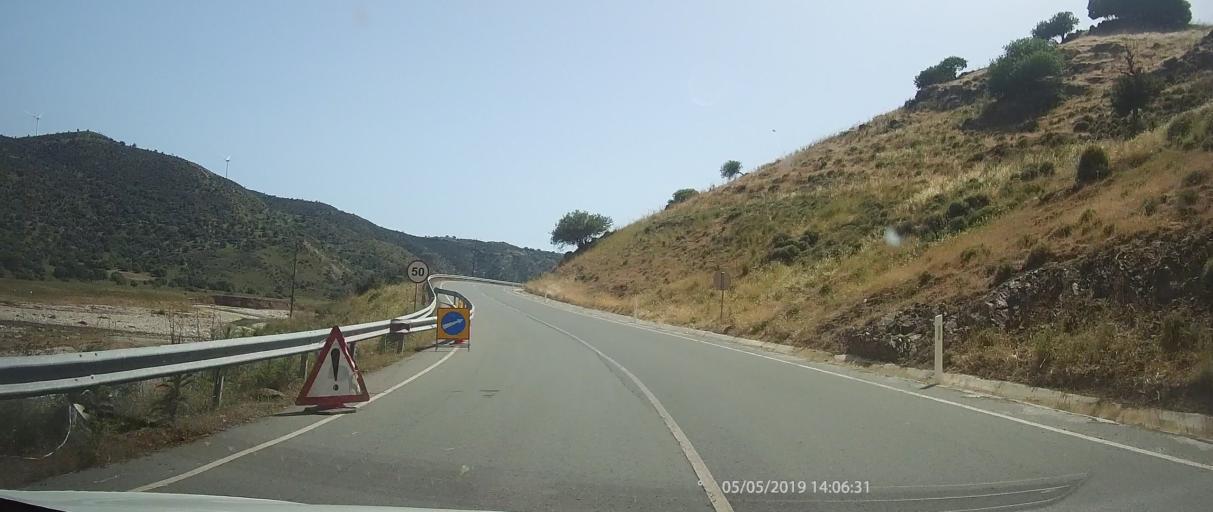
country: CY
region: Limassol
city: Pissouri
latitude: 34.7427
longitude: 32.6052
